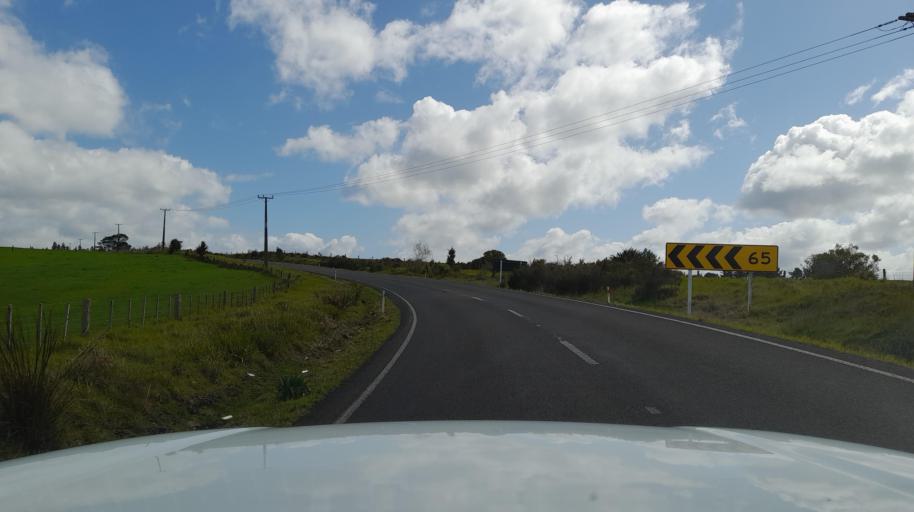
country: NZ
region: Northland
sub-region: Far North District
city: Waimate North
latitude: -35.2700
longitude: 173.8659
